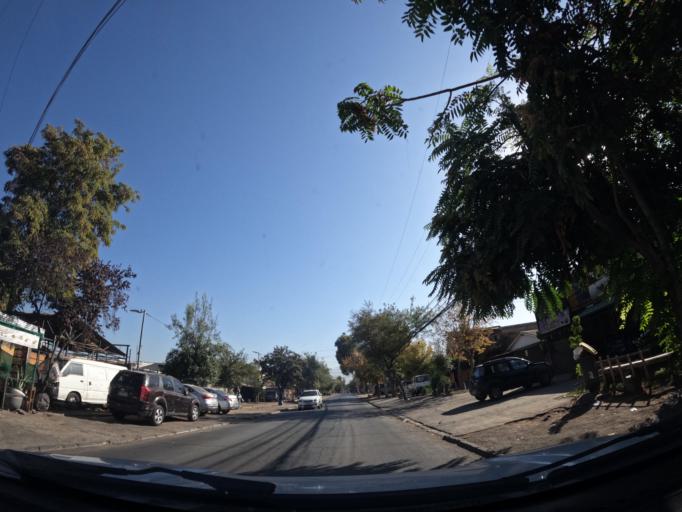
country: CL
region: Santiago Metropolitan
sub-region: Provincia de Santiago
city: Villa Presidente Frei, Nunoa, Santiago, Chile
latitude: -33.4683
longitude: -70.5615
